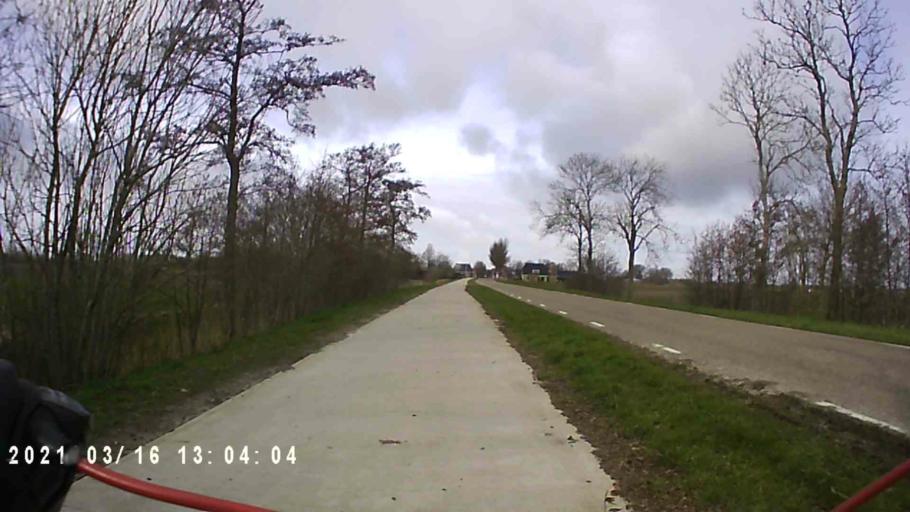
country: NL
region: Friesland
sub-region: Menameradiel
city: Berltsum
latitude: 53.2503
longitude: 5.6334
